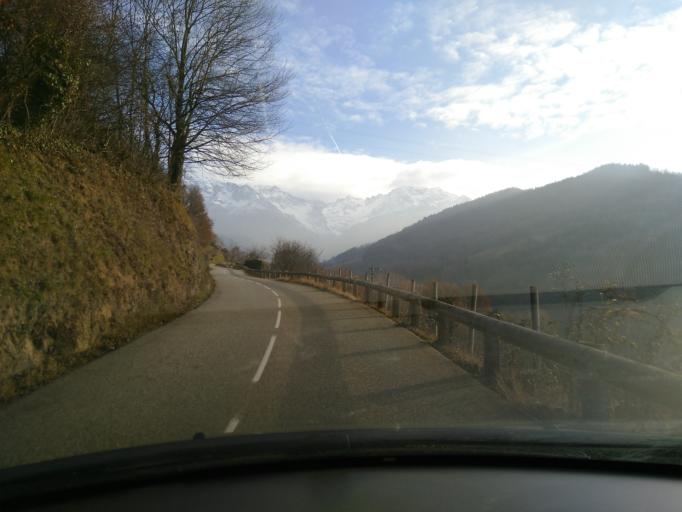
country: FR
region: Rhone-Alpes
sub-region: Departement de l'Isere
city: Villard-Bonnot
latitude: 45.2436
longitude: 5.9061
